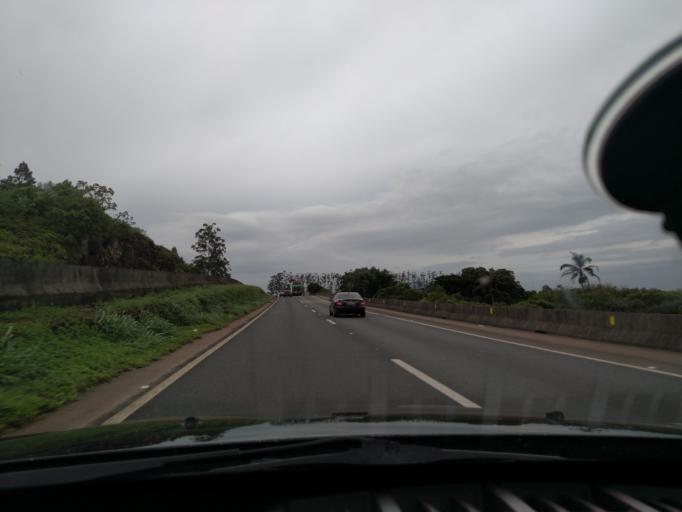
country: BR
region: Santa Catarina
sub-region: Tijucas
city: Tijucas
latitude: -27.3347
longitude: -48.6269
